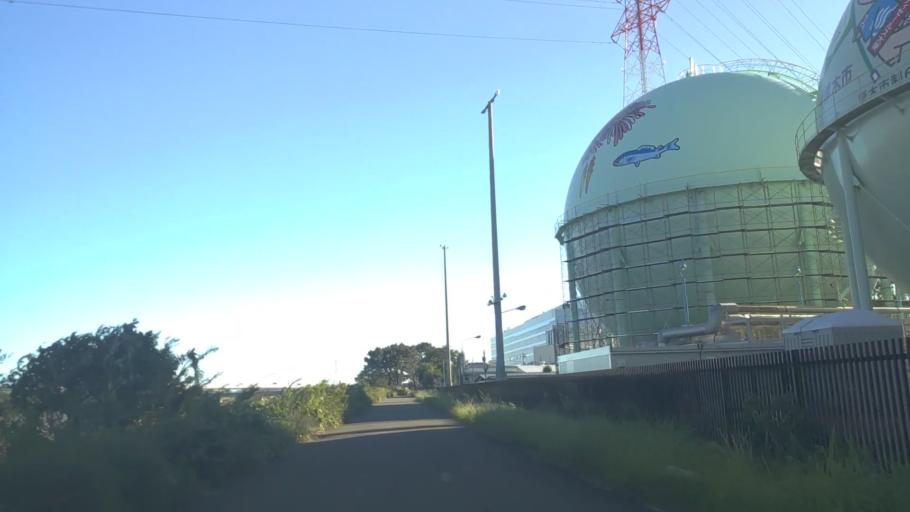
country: JP
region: Kanagawa
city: Atsugi
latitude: 35.4310
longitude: 139.3712
